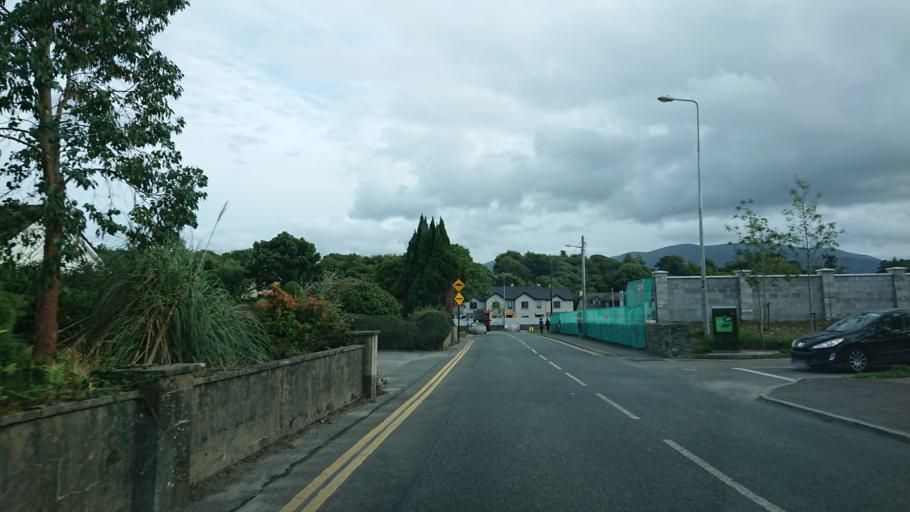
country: IE
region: Munster
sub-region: Ciarrai
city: Cill Airne
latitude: 52.0539
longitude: -9.4890
